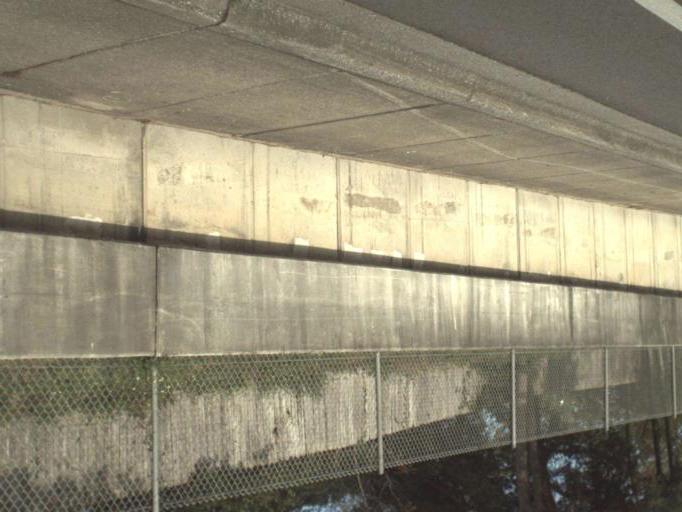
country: US
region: Florida
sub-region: Okaloosa County
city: Niceville
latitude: 30.5083
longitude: -86.4416
